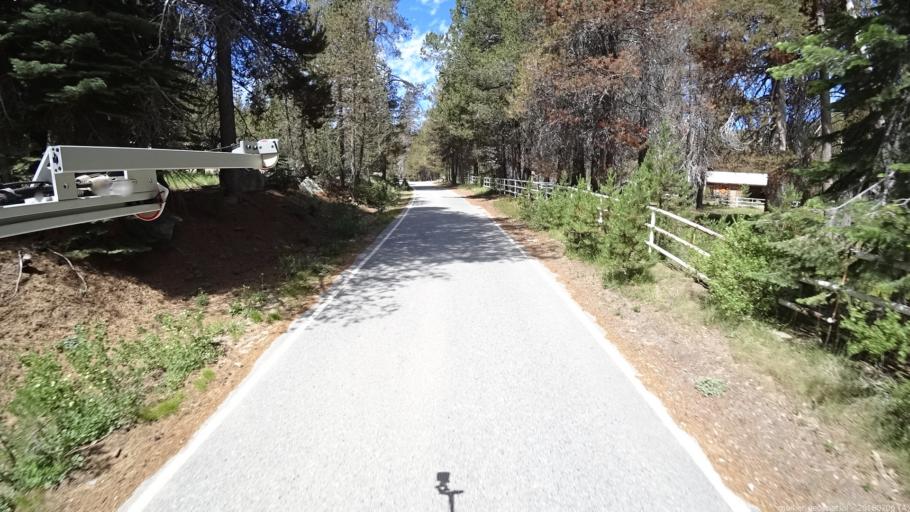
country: US
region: California
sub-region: Madera County
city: Oakhurst
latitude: 37.4449
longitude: -119.4707
